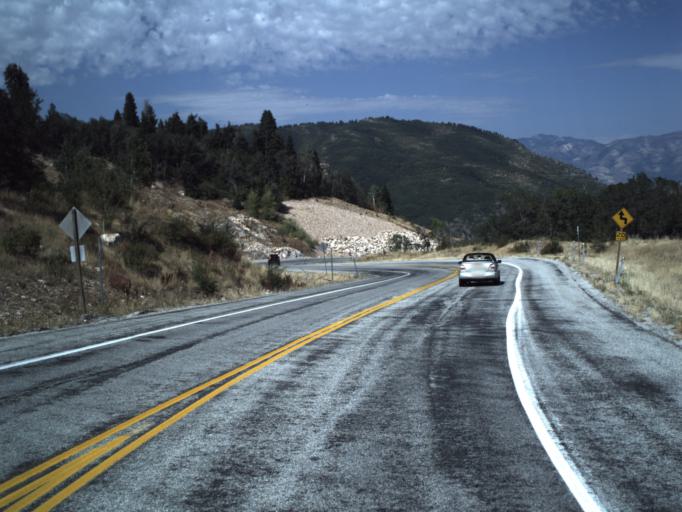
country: US
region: Utah
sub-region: Morgan County
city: Mountain Green
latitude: 41.2133
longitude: -111.8522
